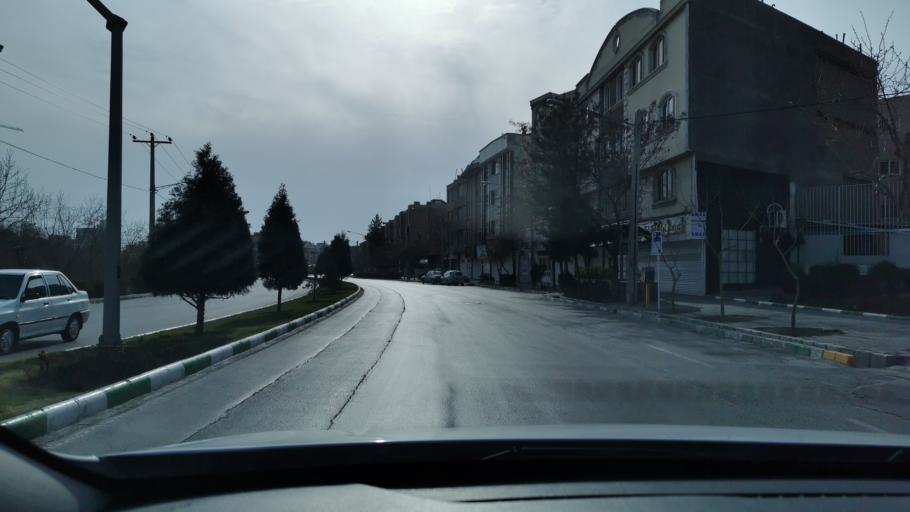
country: IR
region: Razavi Khorasan
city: Mashhad
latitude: 36.3140
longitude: 59.5121
